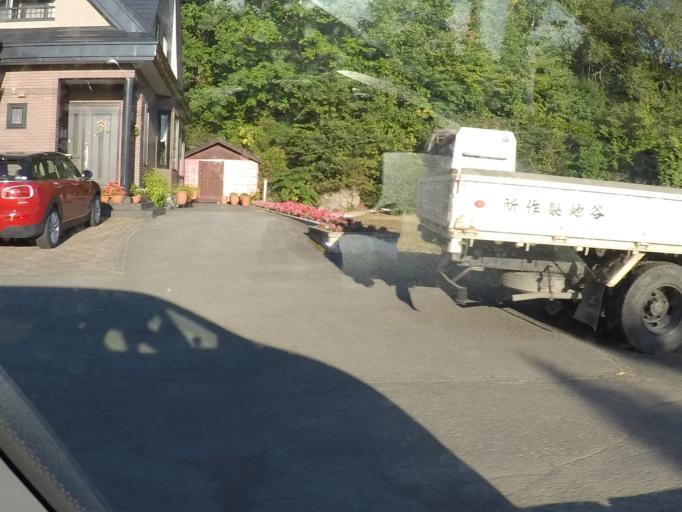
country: JP
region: Hokkaido
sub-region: Asahikawa-shi
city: Asahikawa
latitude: 43.6157
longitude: 142.4798
